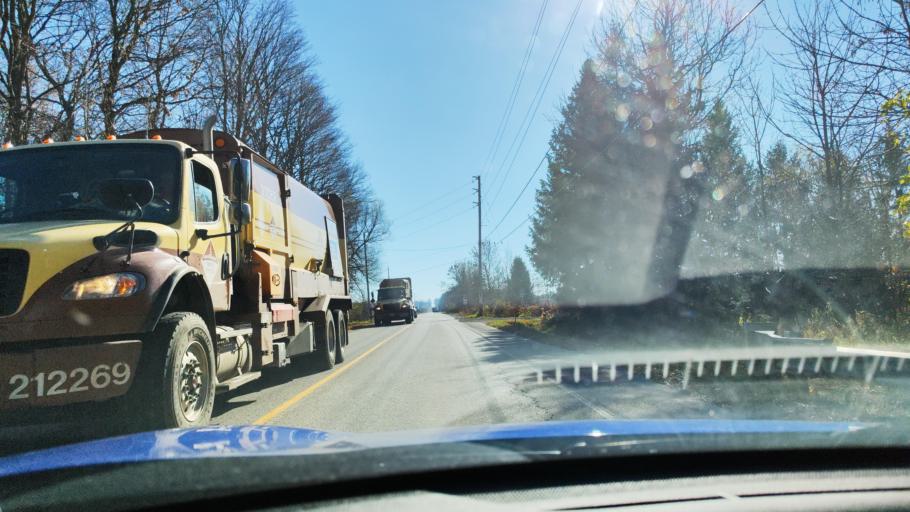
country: CA
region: Ontario
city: Wasaga Beach
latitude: 44.4719
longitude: -80.0063
